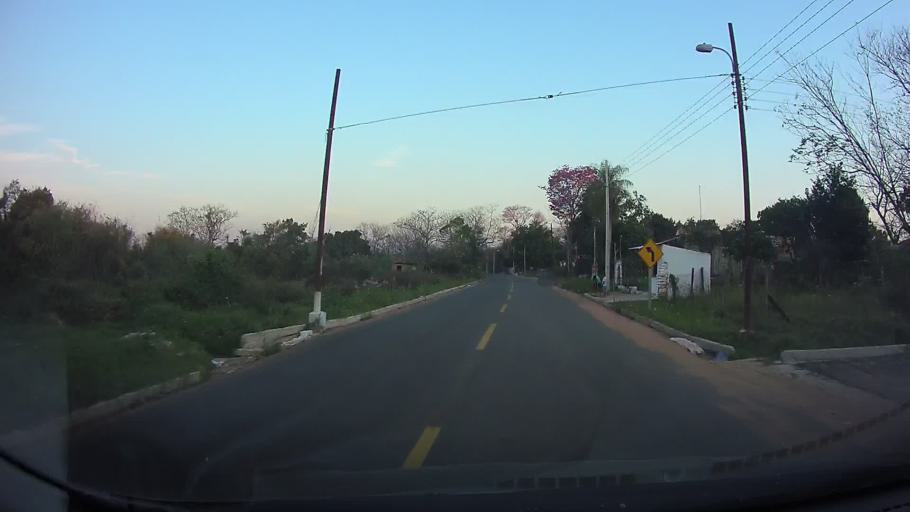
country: PY
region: Central
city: Limpio
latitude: -25.2395
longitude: -57.4958
